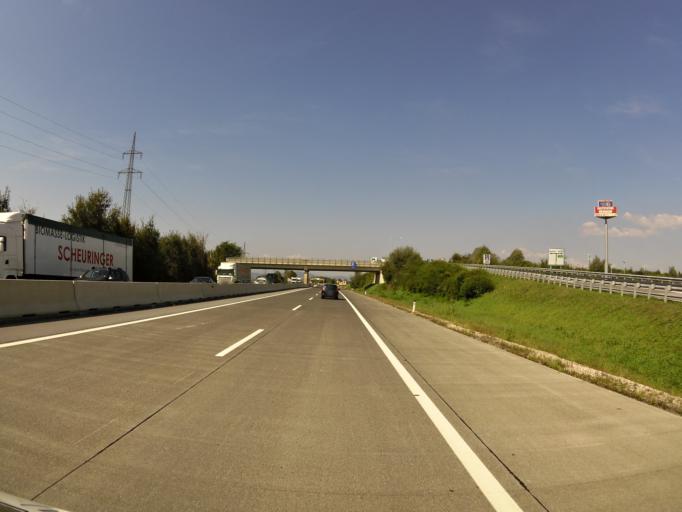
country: AT
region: Styria
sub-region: Politischer Bezirk Graz-Umgebung
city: Wundschuh
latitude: 46.9311
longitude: 15.4649
